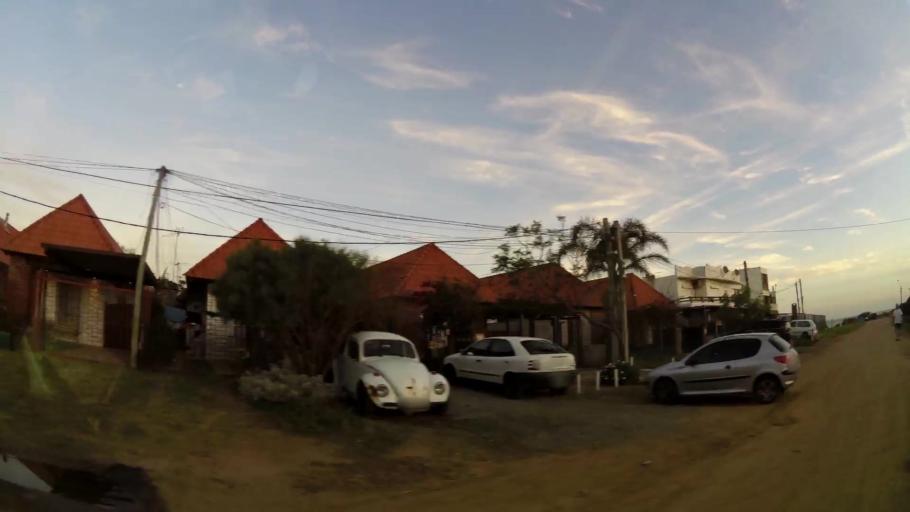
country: UY
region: Canelones
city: Atlantida
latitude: -34.7778
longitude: -55.7492
